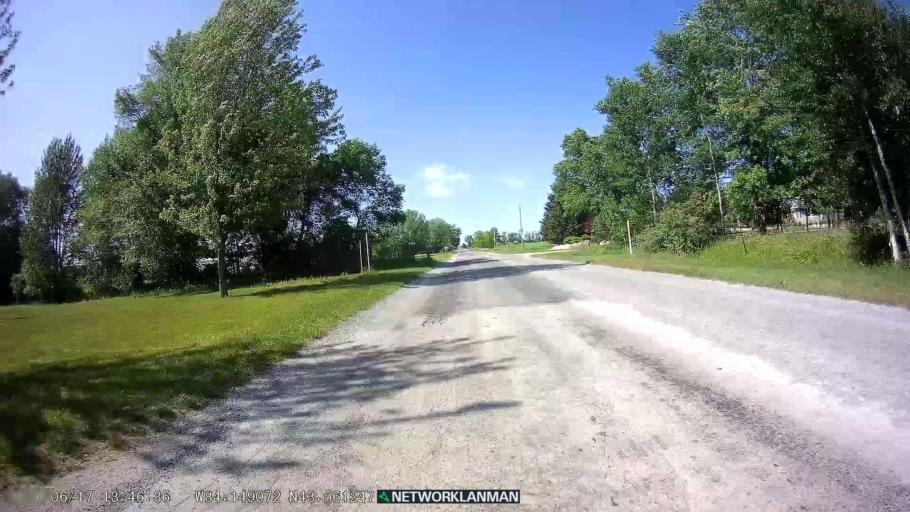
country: US
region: Michigan
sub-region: Saginaw County
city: Freeland
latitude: 43.5609
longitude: -84.1490
